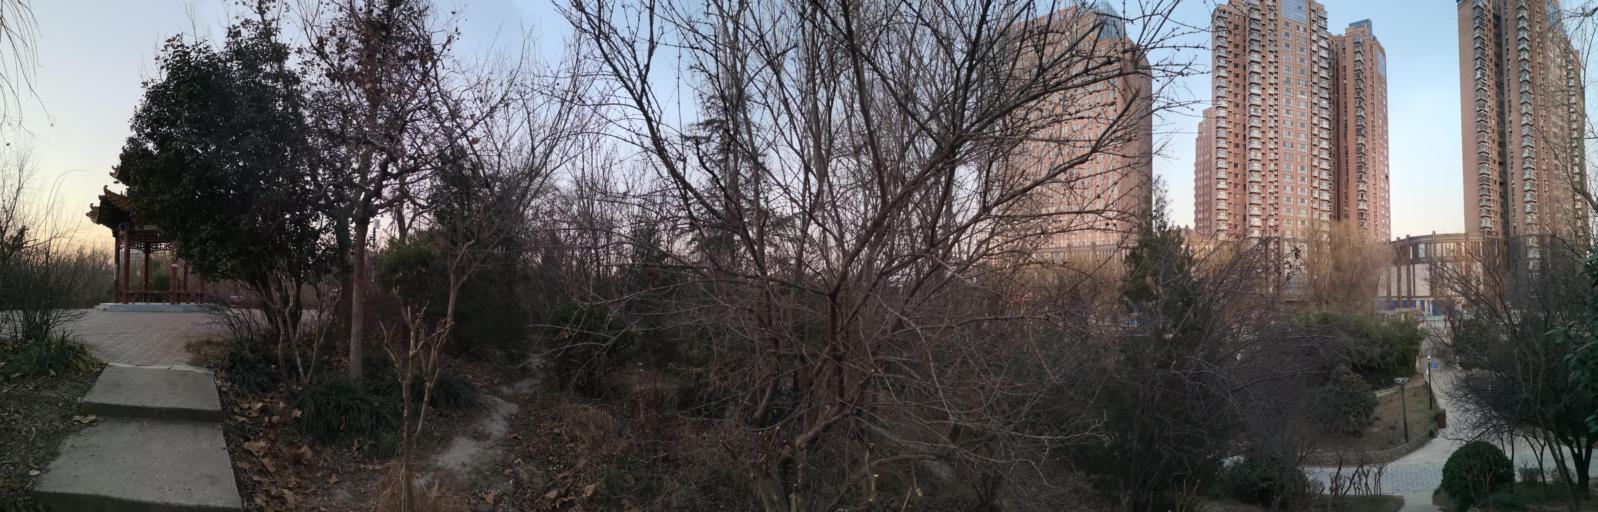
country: CN
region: Henan Sheng
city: Zhongyuanlu
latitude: 35.7737
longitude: 115.0786
